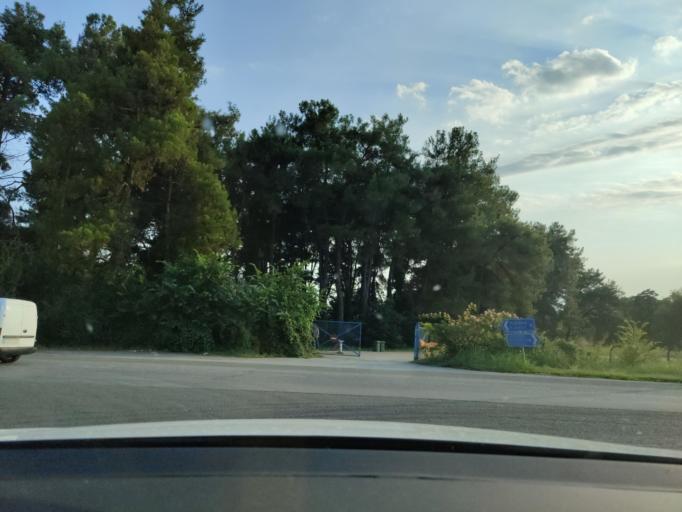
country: GR
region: East Macedonia and Thrace
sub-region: Nomos Kavalas
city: Amygdaleonas
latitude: 40.9706
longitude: 24.3521
